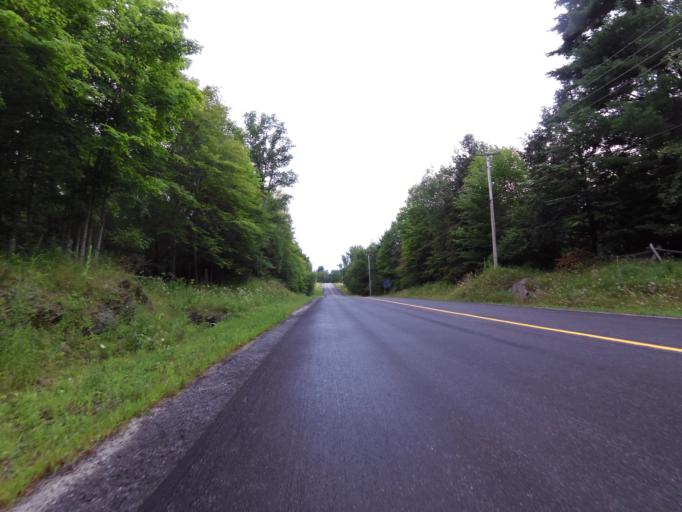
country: CA
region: Ontario
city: Perth
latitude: 45.0634
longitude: -76.3911
